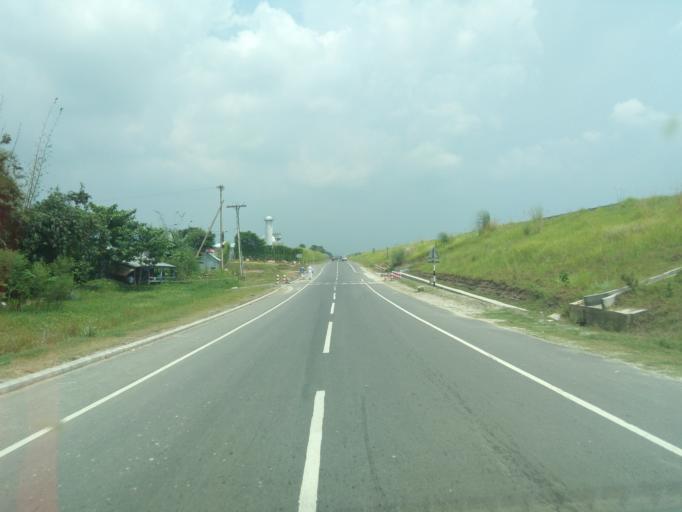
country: BD
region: Dhaka
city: Char Bhadrasan
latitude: 23.3996
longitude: 90.2161
